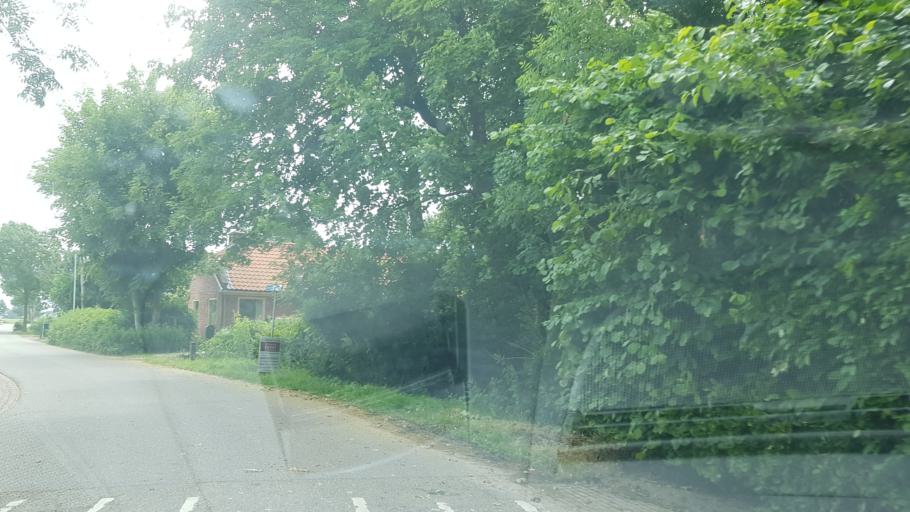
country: NL
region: Groningen
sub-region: Gemeente Winsum
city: Winsum
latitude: 53.4007
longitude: 6.4772
